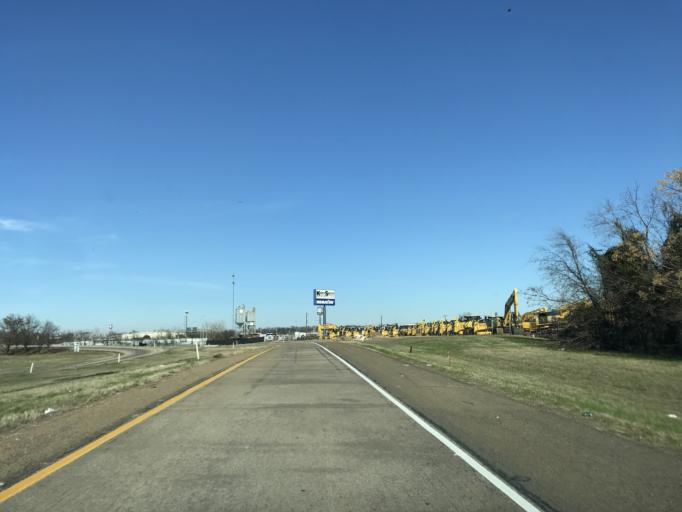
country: US
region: Texas
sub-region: Dallas County
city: Hutchins
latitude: 32.6993
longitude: -96.7512
